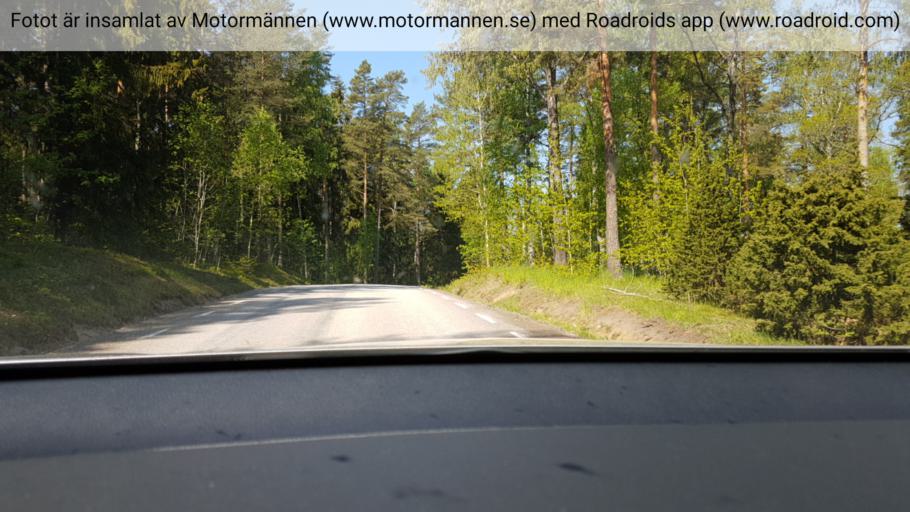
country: SE
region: Kalmar
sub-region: Vasterviks Kommun
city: Vaestervik
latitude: 57.8262
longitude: 16.5586
